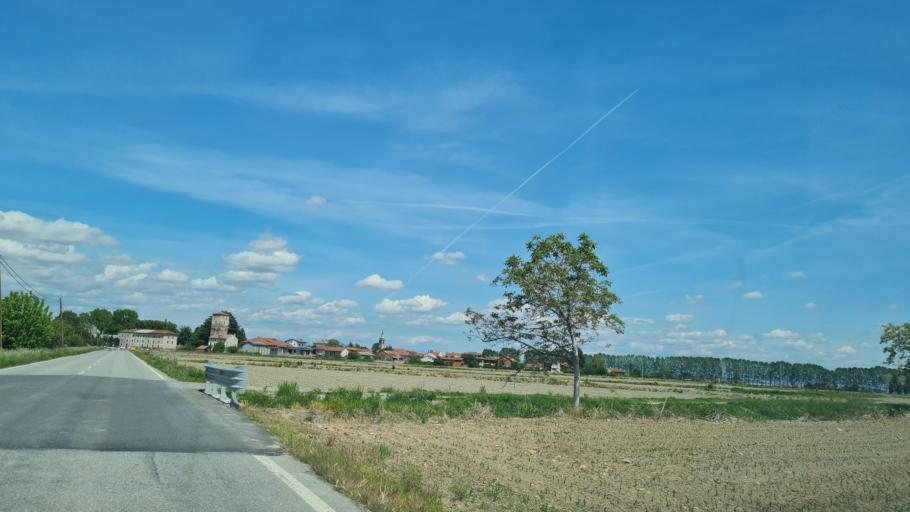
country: IT
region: Piedmont
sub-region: Provincia di Novara
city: Mandello Vitta
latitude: 45.4897
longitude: 8.4586
